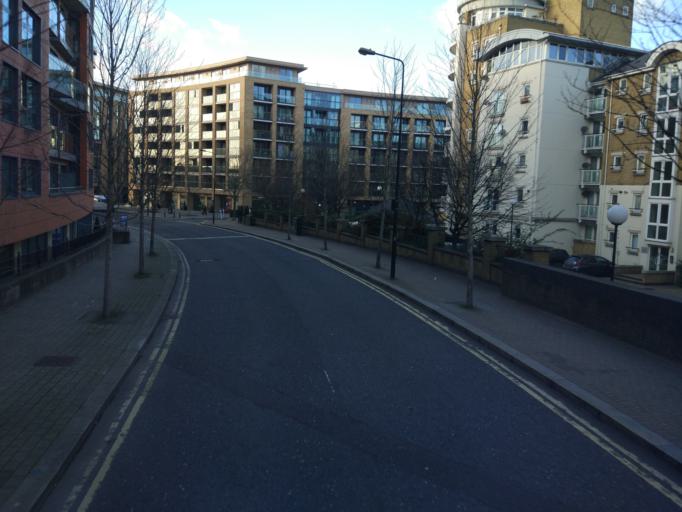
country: GB
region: England
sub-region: Greater London
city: Bethnal Green
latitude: 51.4988
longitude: -0.0473
